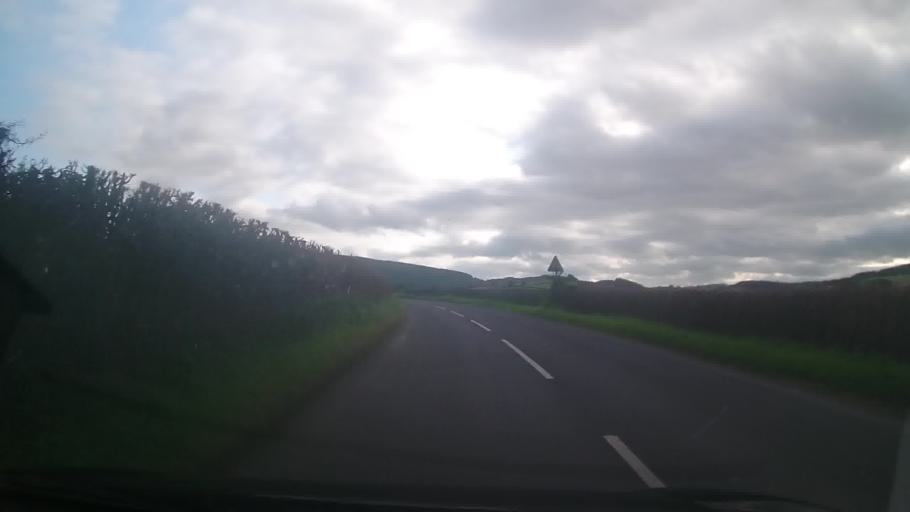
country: GB
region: England
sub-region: Shropshire
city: Bishop's Castle
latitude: 52.4741
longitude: -2.9935
